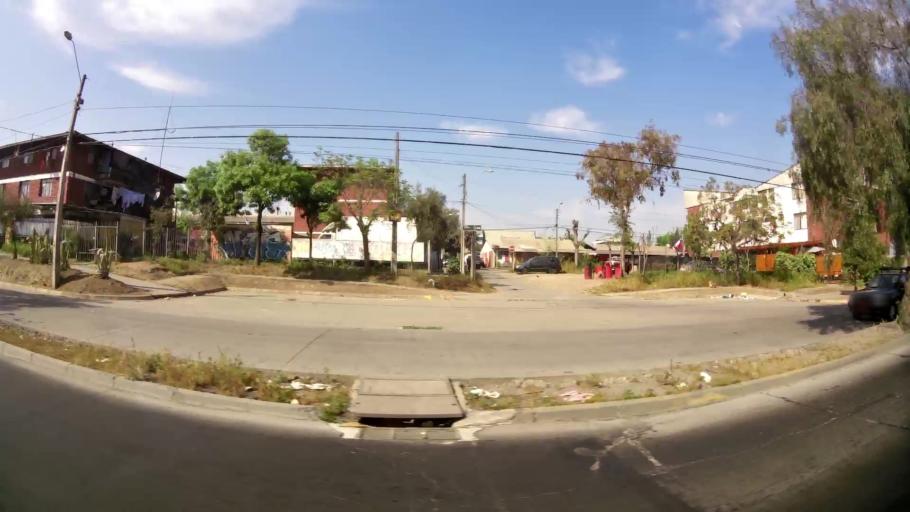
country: CL
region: Santiago Metropolitan
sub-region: Provincia de Santiago
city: Lo Prado
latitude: -33.4448
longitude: -70.7463
